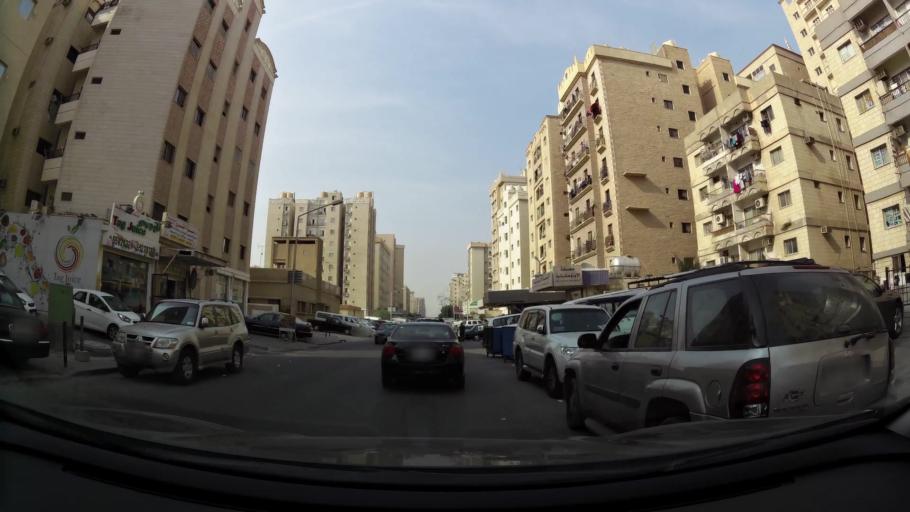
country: KW
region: Al Farwaniyah
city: Al Farwaniyah
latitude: 29.2742
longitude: 47.9562
